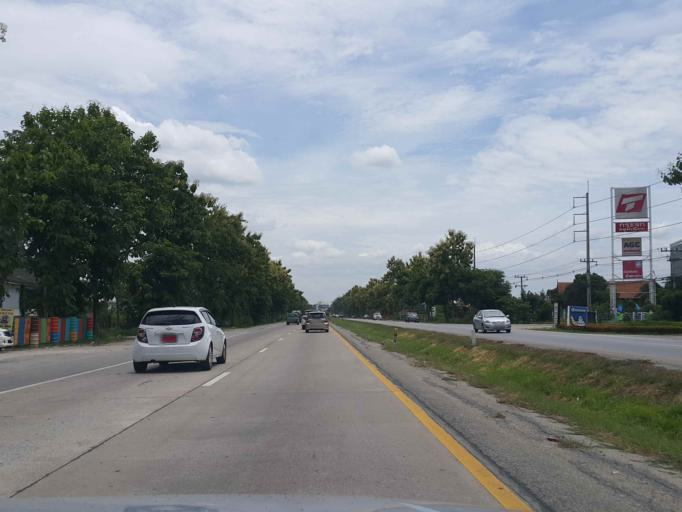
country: TH
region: Chiang Mai
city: Saraphi
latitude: 18.7101
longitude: 99.0453
